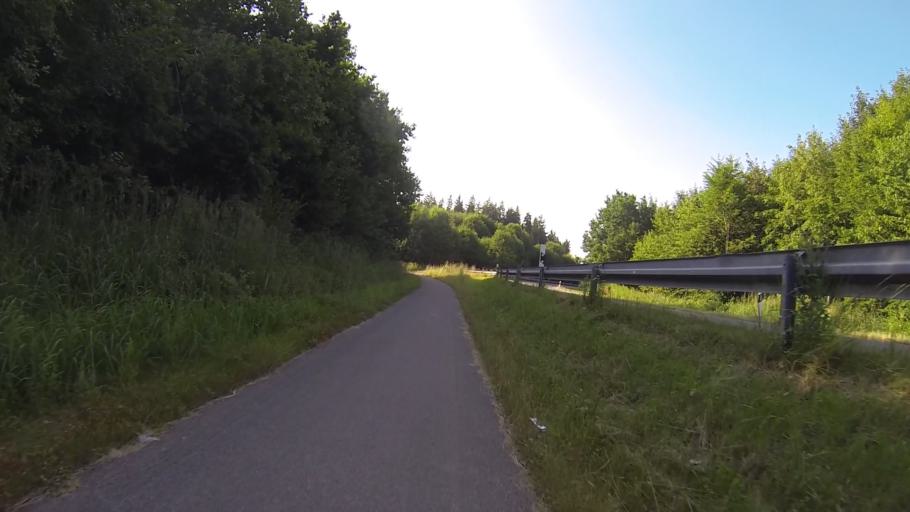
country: DE
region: Baden-Wuerttemberg
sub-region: Tuebingen Region
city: Staig
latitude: 48.3113
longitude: 9.9685
